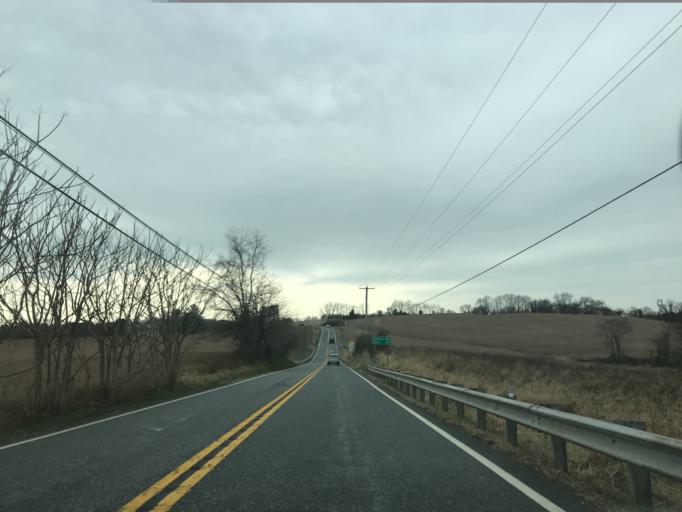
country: US
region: Maryland
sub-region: Harford County
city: Bel Air North
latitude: 39.5990
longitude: -76.3424
